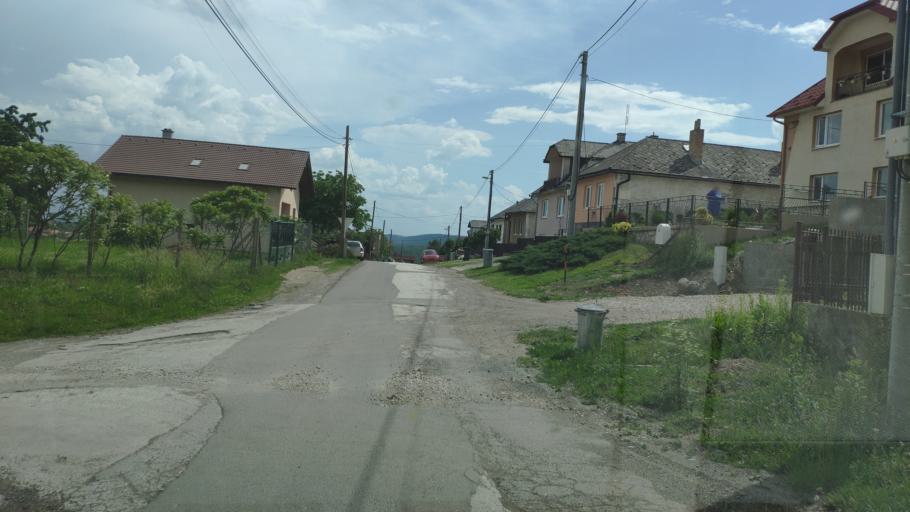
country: SK
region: Kosicky
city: Medzev
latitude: 48.7142
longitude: 20.9741
